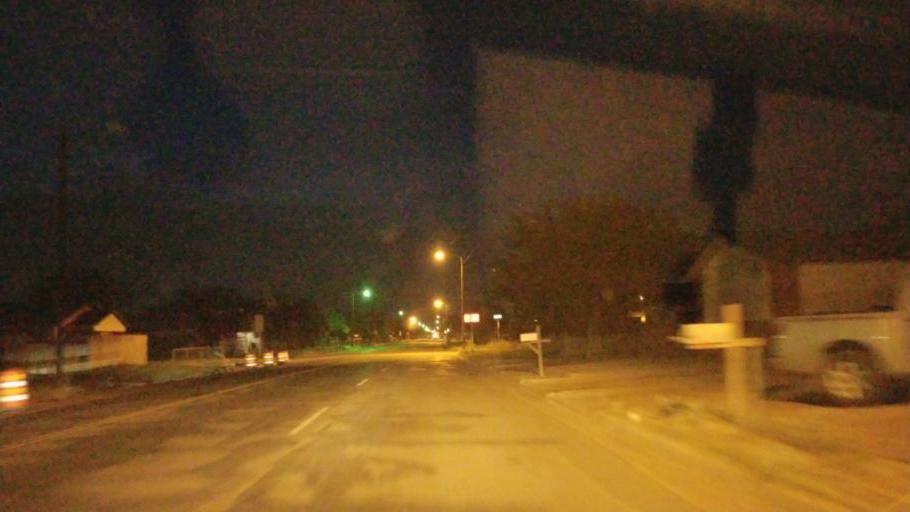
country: US
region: Texas
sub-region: Potter County
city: Amarillo
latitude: 35.1932
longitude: -101.8270
